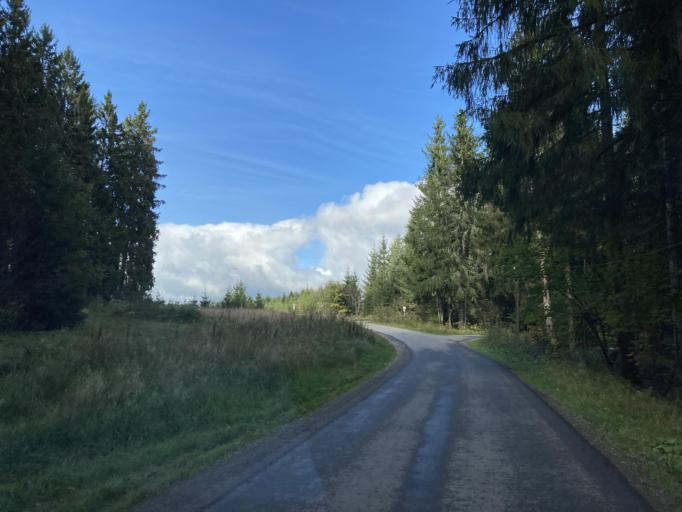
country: DE
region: Baden-Wuerttemberg
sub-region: Freiburg Region
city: Vohrenbach
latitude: 48.0781
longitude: 8.2814
